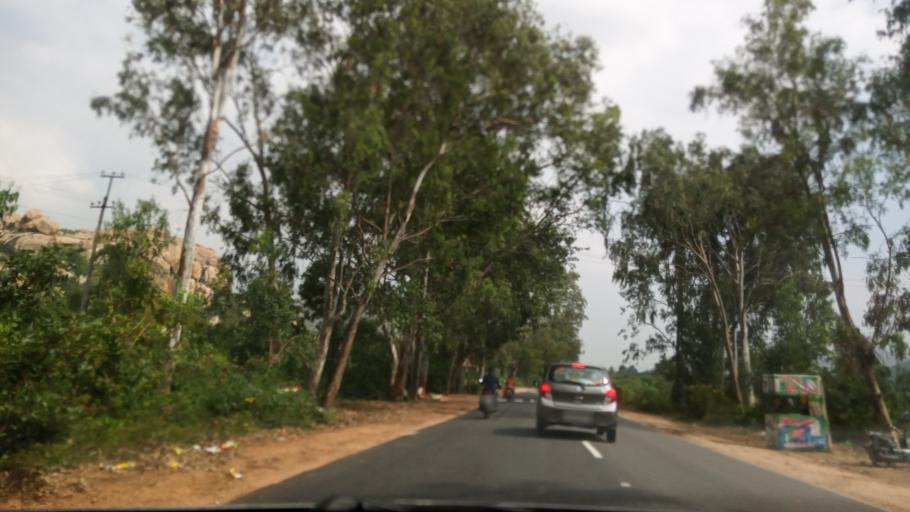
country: IN
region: Andhra Pradesh
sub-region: Chittoor
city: Madanapalle
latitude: 13.6355
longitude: 78.6053
